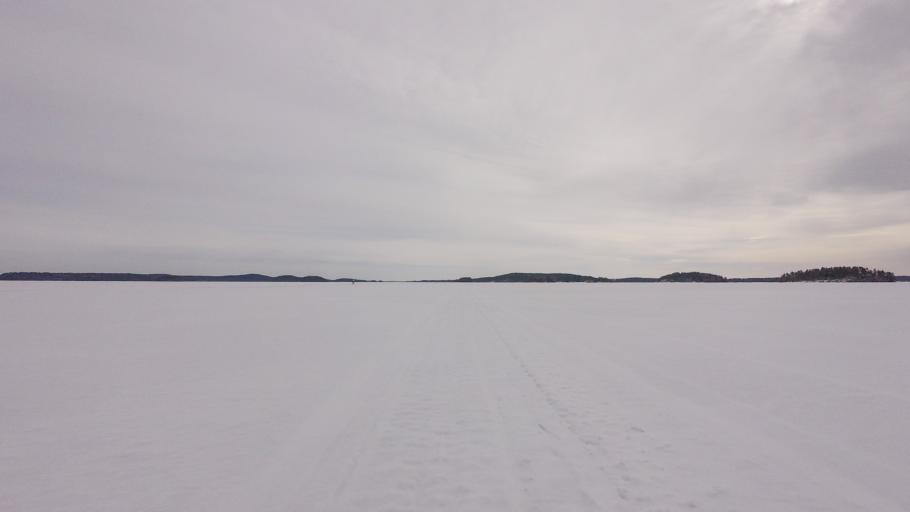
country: FI
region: Southern Savonia
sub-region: Savonlinna
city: Rantasalmi
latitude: 62.1047
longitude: 28.4231
